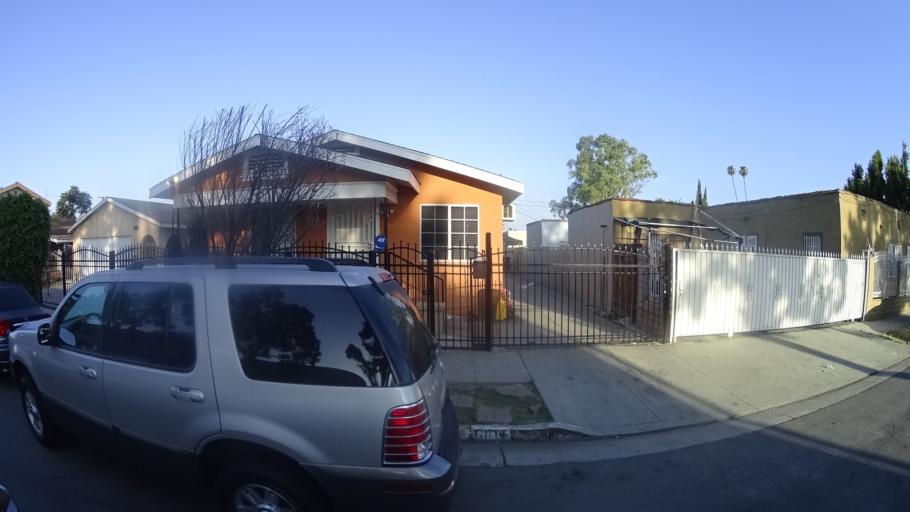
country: US
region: California
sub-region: Los Angeles County
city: Westmont
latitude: 33.9780
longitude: -118.2849
